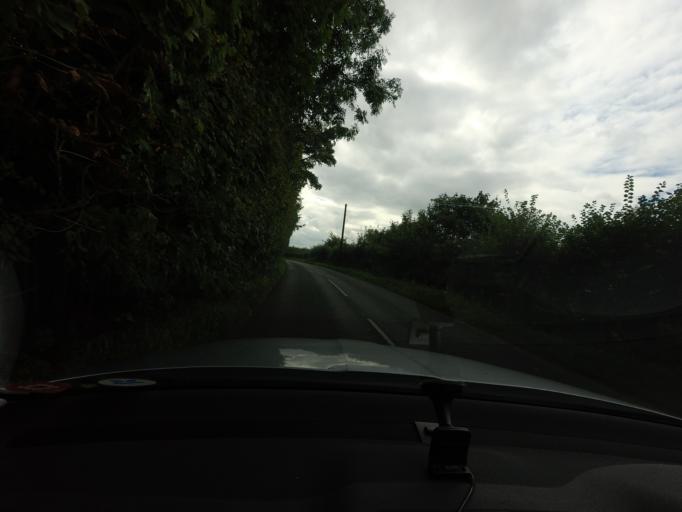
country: GB
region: England
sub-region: Kent
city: Borough Green
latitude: 51.2955
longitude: 0.2845
